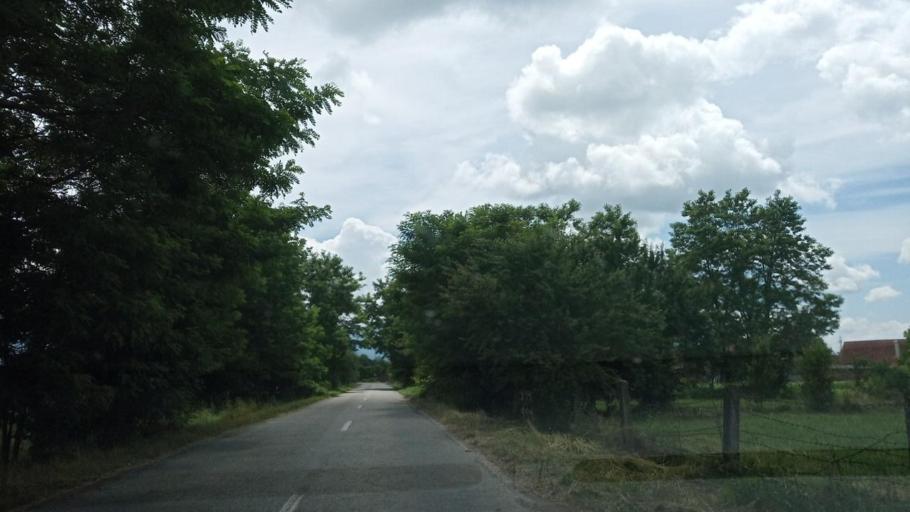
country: RO
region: Sibiu
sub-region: Comuna Porumbacu de Jos
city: Porumbacu de Jos
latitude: 45.7518
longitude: 24.4612
